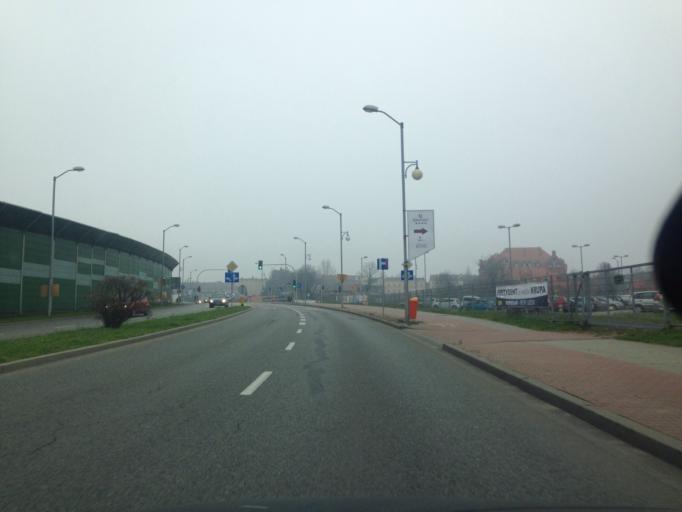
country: PL
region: Silesian Voivodeship
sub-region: Katowice
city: Katowice
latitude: 50.2612
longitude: 19.0350
